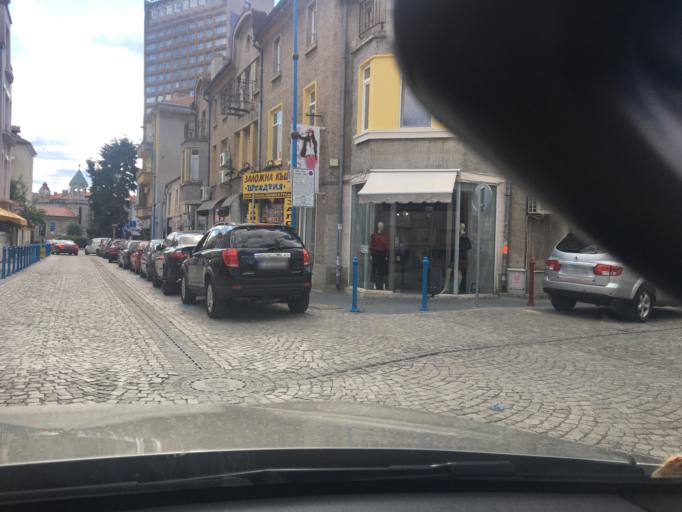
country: BG
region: Burgas
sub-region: Obshtina Burgas
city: Burgas
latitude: 42.4943
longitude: 27.4743
